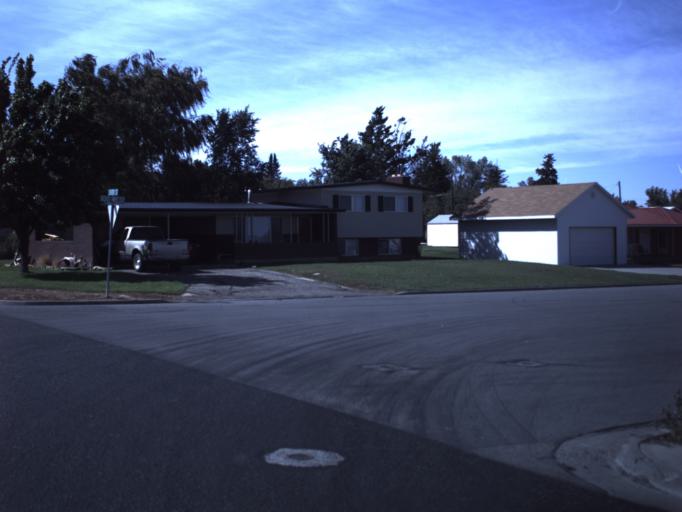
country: US
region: Utah
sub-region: San Juan County
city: Monticello
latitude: 37.8727
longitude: -109.3445
